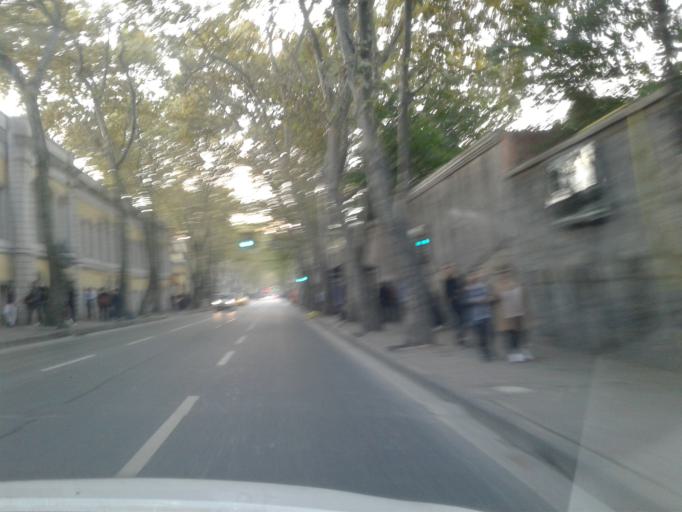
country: TR
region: Istanbul
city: UEskuedar
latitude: 41.0466
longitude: 29.0213
